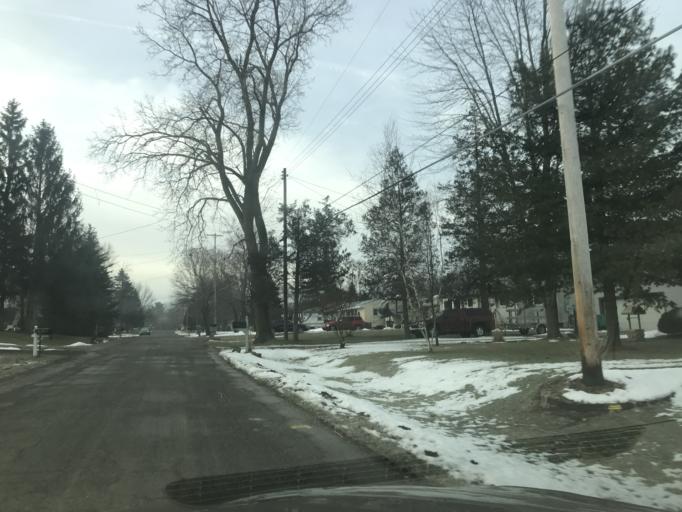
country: US
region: Michigan
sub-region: Ingham County
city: Lansing
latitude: 42.7865
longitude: -84.5497
